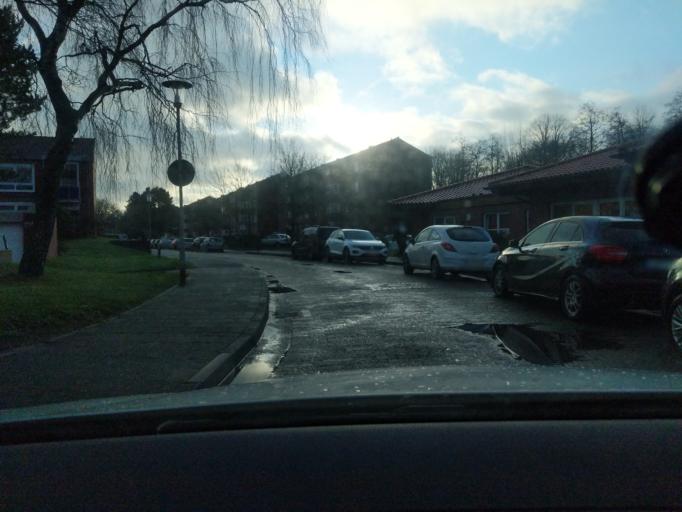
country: DE
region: Lower Saxony
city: Cuxhaven
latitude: 53.8540
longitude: 8.6824
